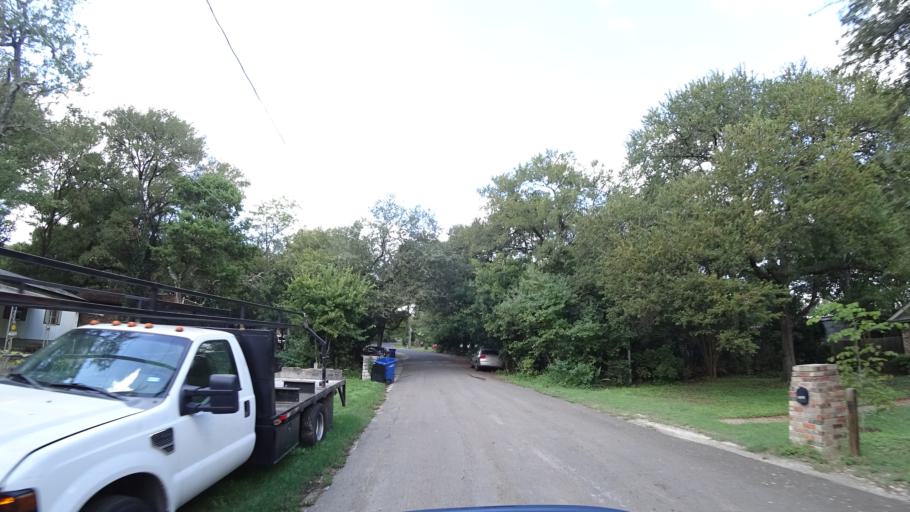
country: US
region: Texas
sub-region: Travis County
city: Manchaca
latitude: 30.1947
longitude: -97.8085
